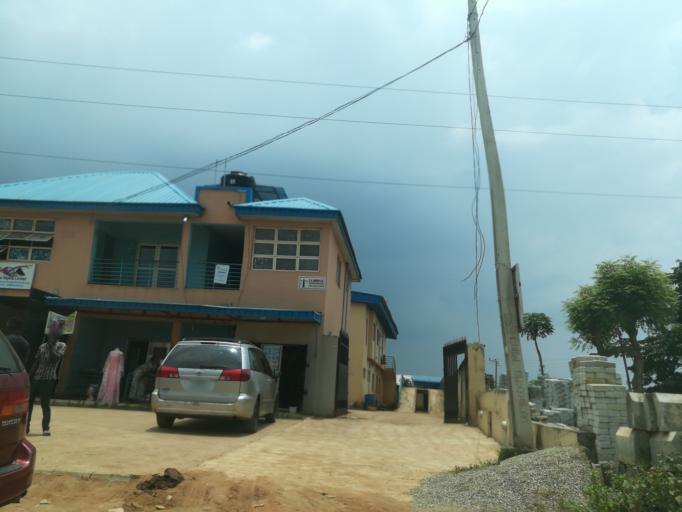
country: NG
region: Lagos
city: Ikorodu
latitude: 6.6133
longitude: 3.5765
